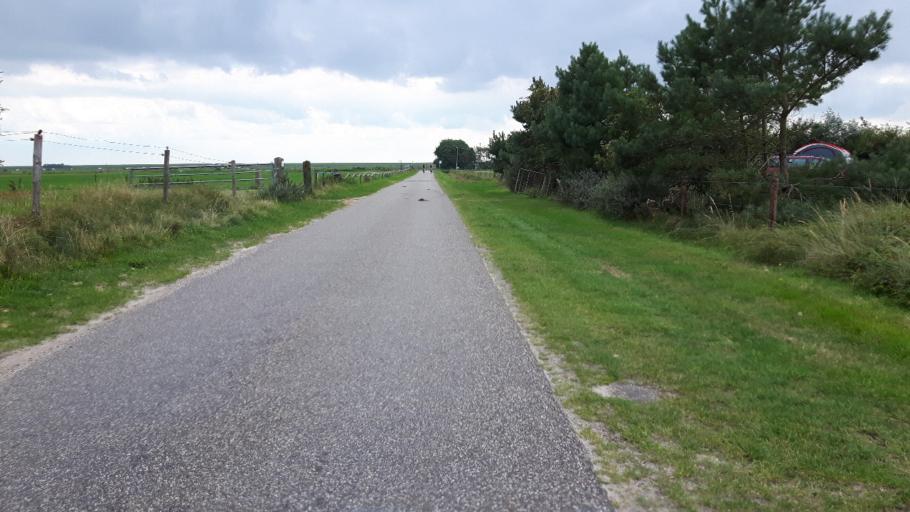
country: NL
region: Friesland
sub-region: Gemeente Ameland
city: Nes
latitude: 53.4514
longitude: 5.8178
